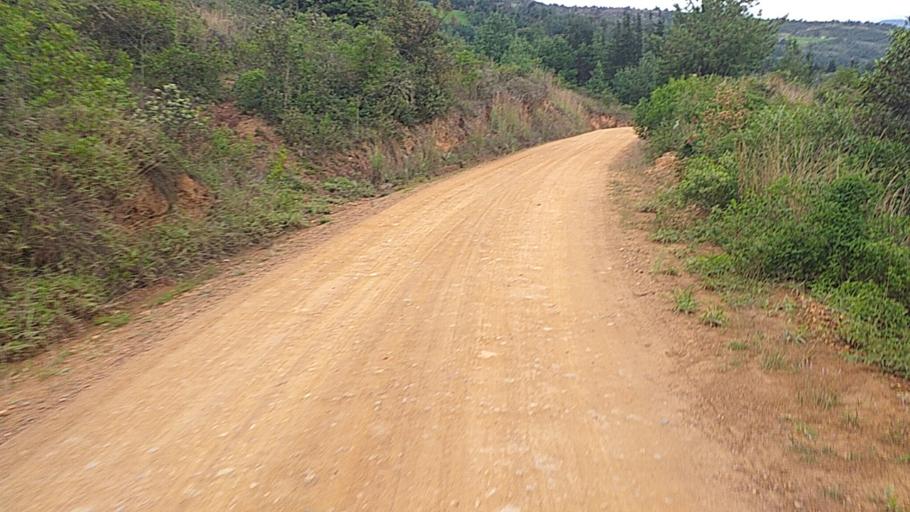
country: CO
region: Boyaca
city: Floresta
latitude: 5.8786
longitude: -72.9125
